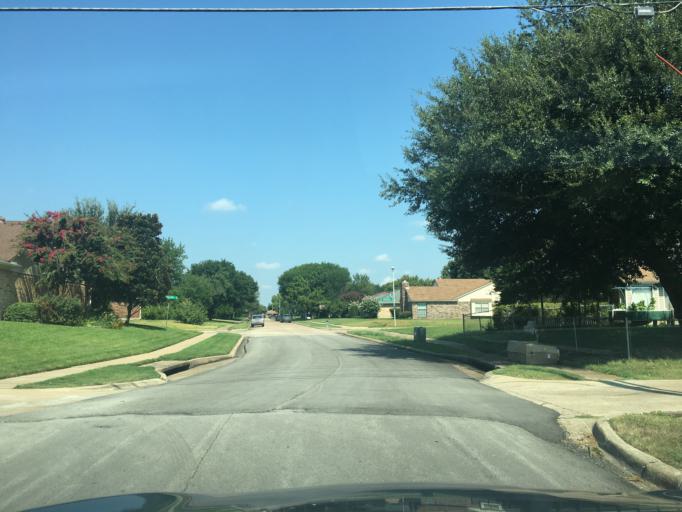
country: US
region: Texas
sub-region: Dallas County
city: Garland
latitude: 32.9463
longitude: -96.6273
